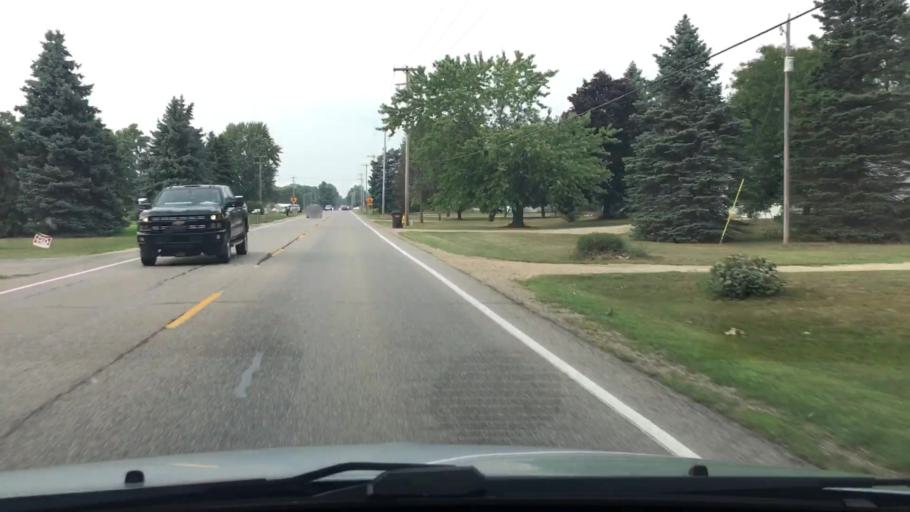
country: US
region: Michigan
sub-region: Ottawa County
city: Hudsonville
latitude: 42.9035
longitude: -85.9020
